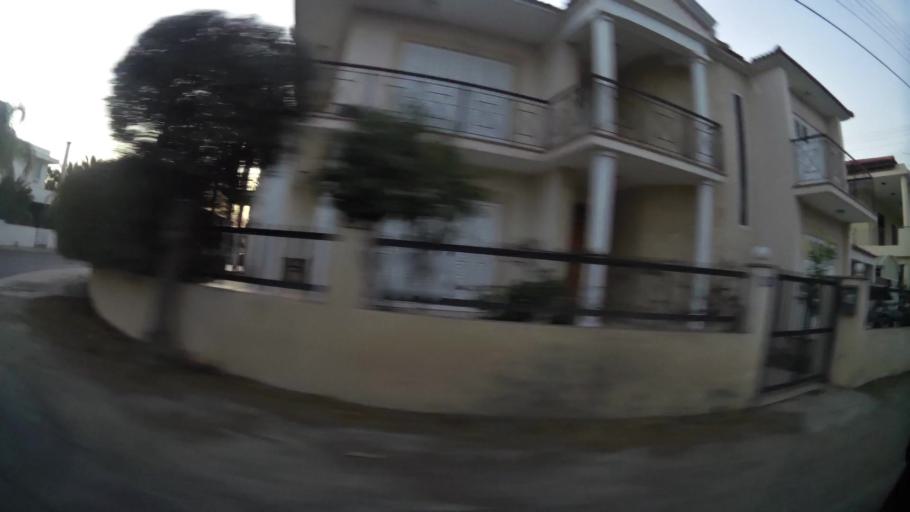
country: CY
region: Lefkosia
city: Nicosia
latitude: 35.1594
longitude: 33.3314
